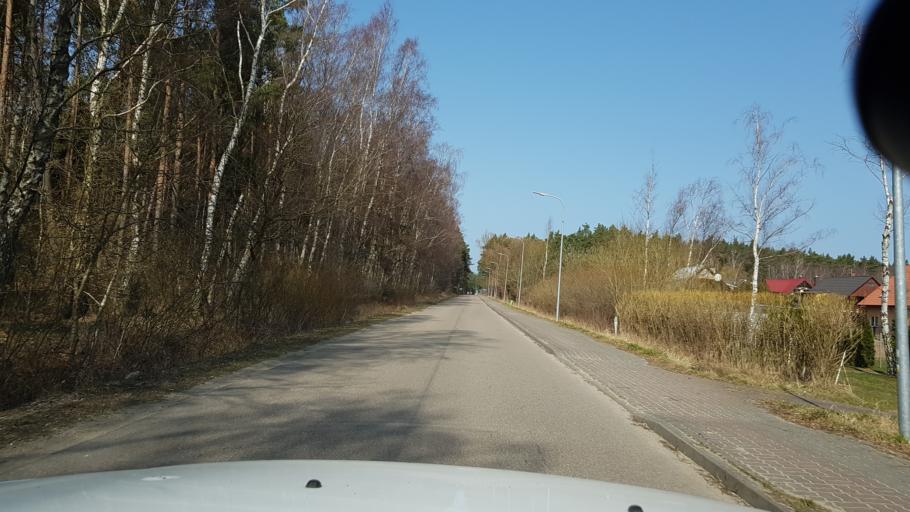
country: PL
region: West Pomeranian Voivodeship
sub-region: Powiat slawienski
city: Darlowo
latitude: 54.5206
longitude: 16.5130
